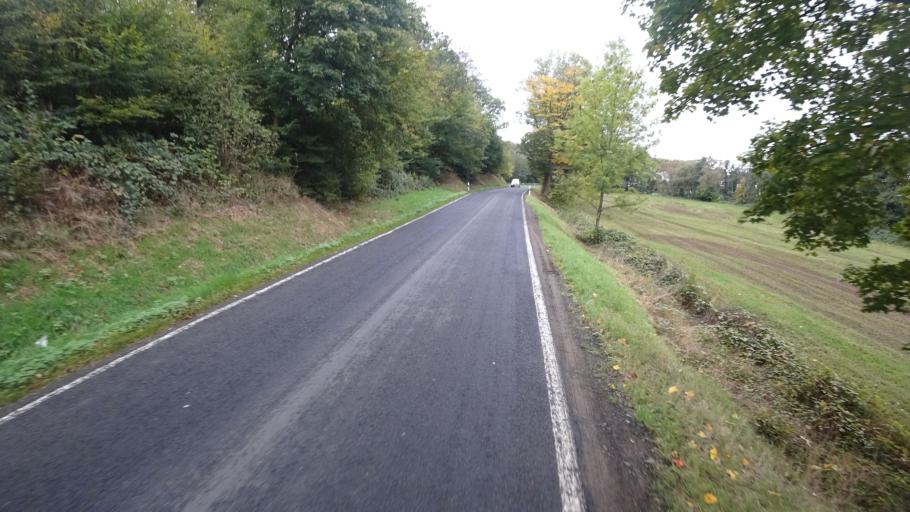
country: DE
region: Rheinland-Pfalz
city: Oberhaid
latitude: 50.5106
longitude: 7.7226
